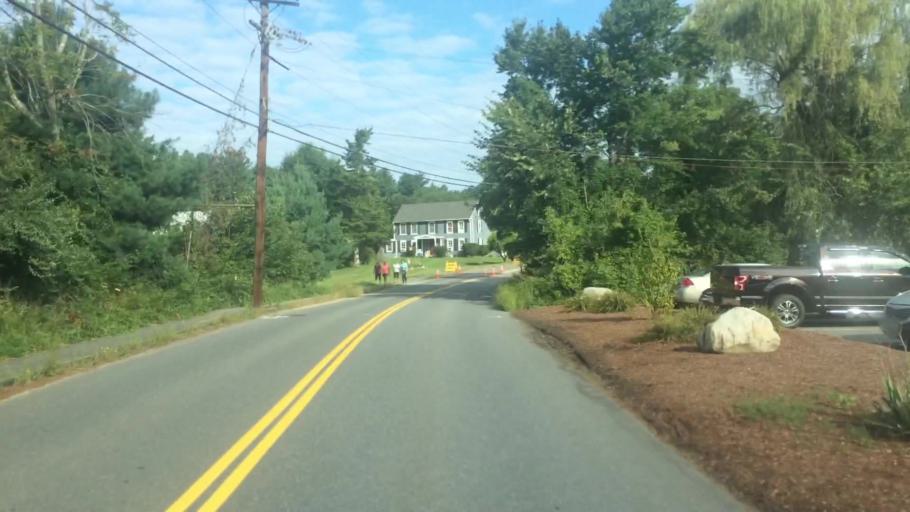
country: US
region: Massachusetts
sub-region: Middlesex County
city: Acton
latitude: 42.4683
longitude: -71.4574
